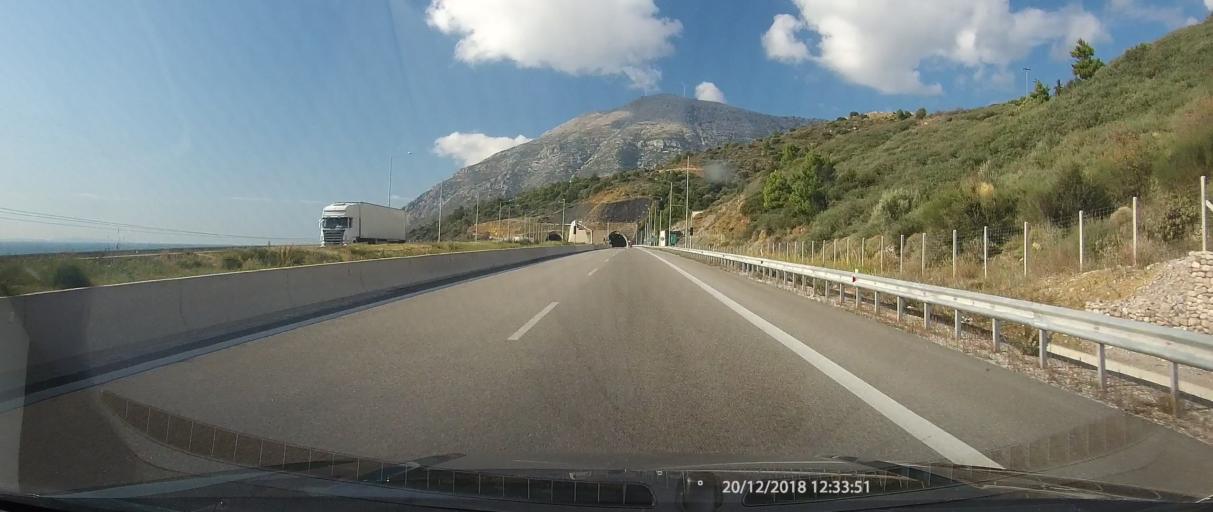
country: GR
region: West Greece
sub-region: Nomos Aitolias kai Akarnanias
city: Antirrio
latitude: 38.3525
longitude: 21.7302
